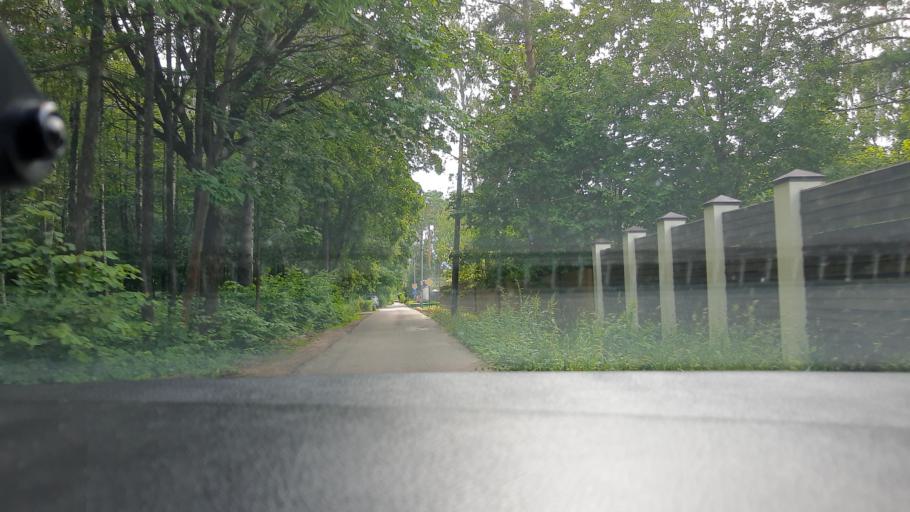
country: RU
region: Moscow
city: Novo-Peredelkino
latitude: 55.6773
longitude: 37.3300
